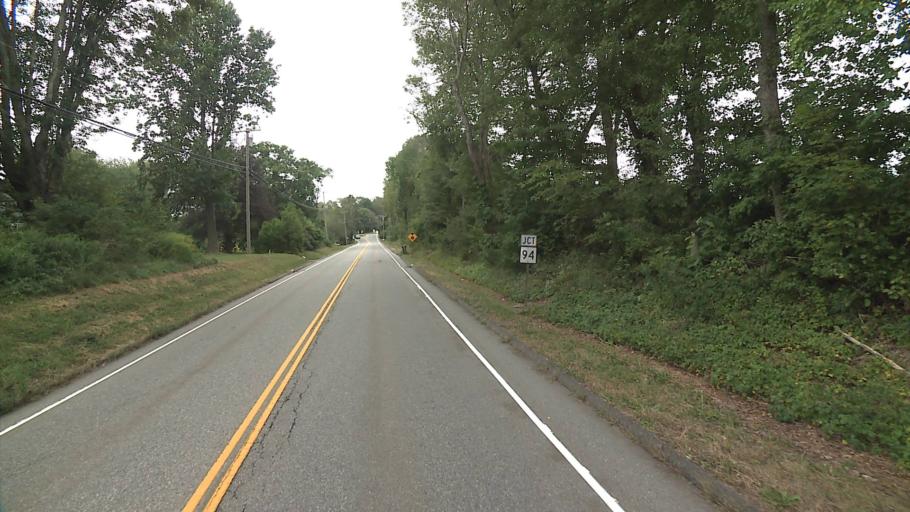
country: US
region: Connecticut
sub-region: Hartford County
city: Terramuggus
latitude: 41.6948
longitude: -72.4375
